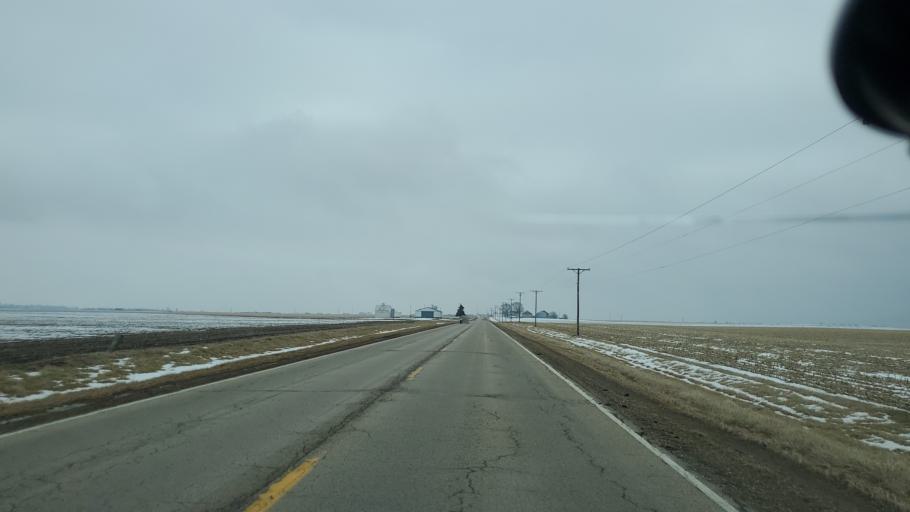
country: US
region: Illinois
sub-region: Marshall County
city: Wenona
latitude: 41.1188
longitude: -89.1029
